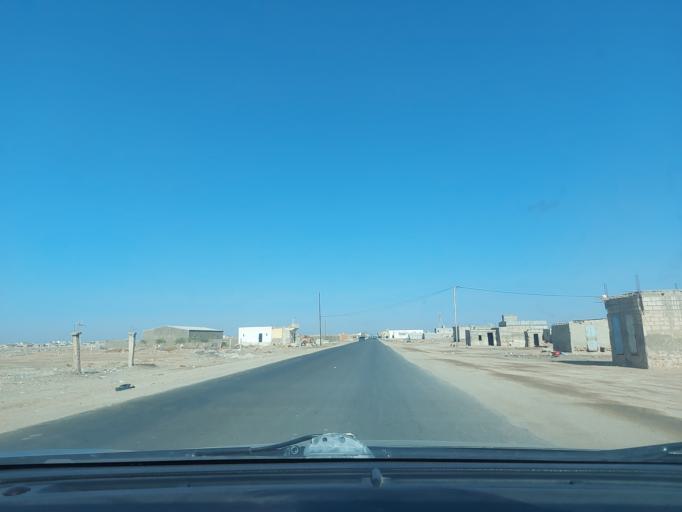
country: MR
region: Nouakchott
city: Nouakchott
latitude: 18.0110
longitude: -15.9823
